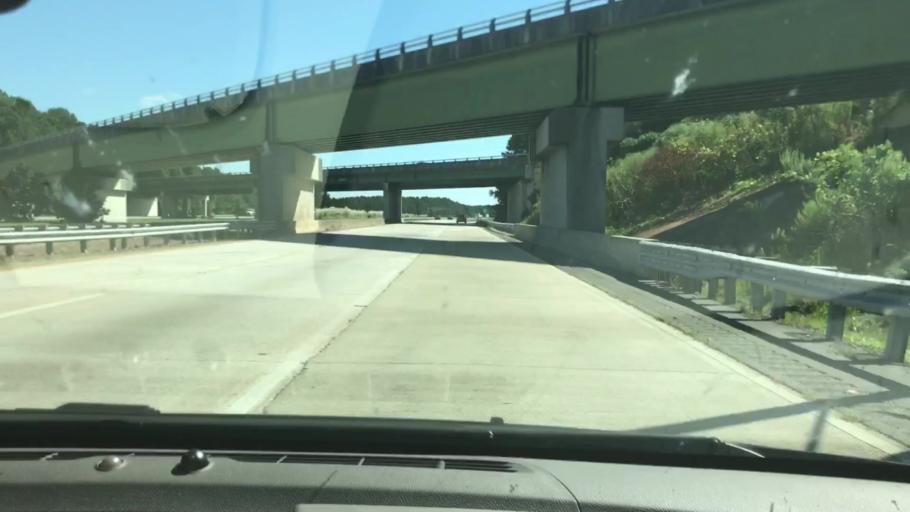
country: US
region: Alabama
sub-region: Russell County
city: Phenix City
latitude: 32.5475
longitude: -84.9525
